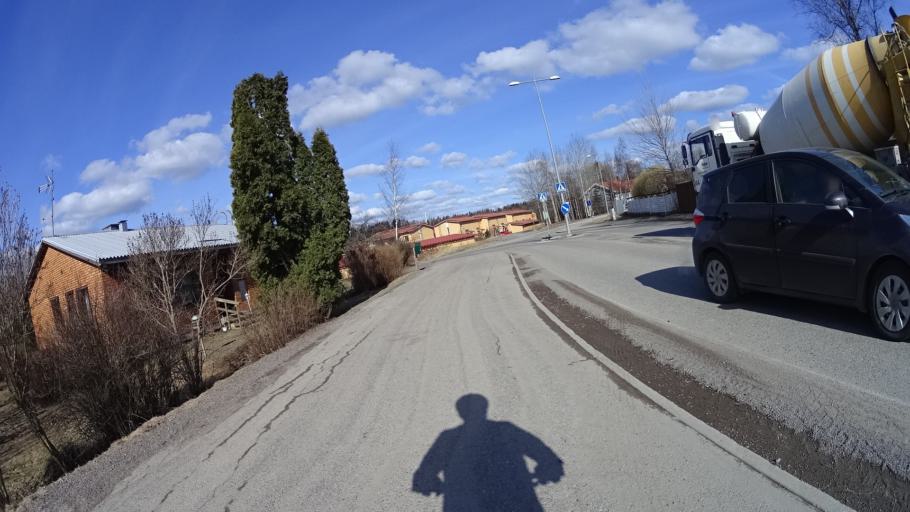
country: FI
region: Uusimaa
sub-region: Helsinki
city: Kauniainen
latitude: 60.2861
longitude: 24.7357
